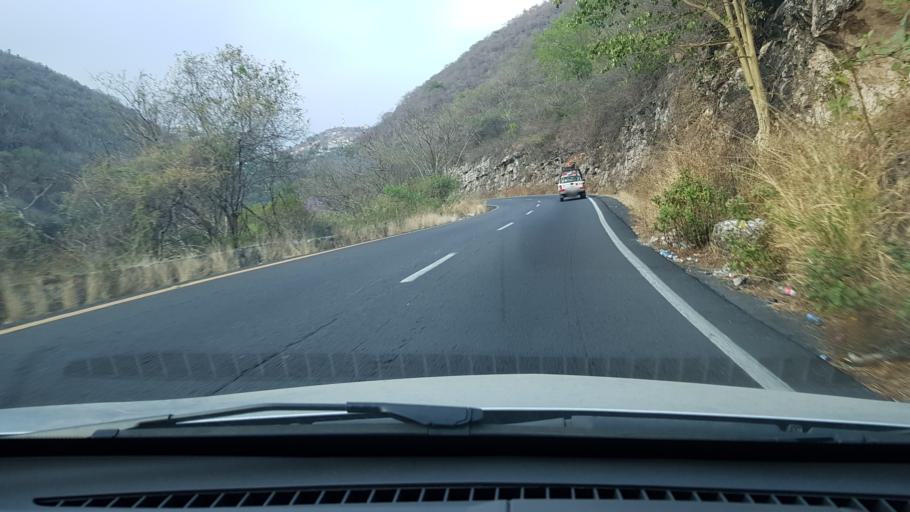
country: MX
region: Morelos
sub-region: Jiutepec
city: Independencia
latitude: 18.8675
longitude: -99.1198
